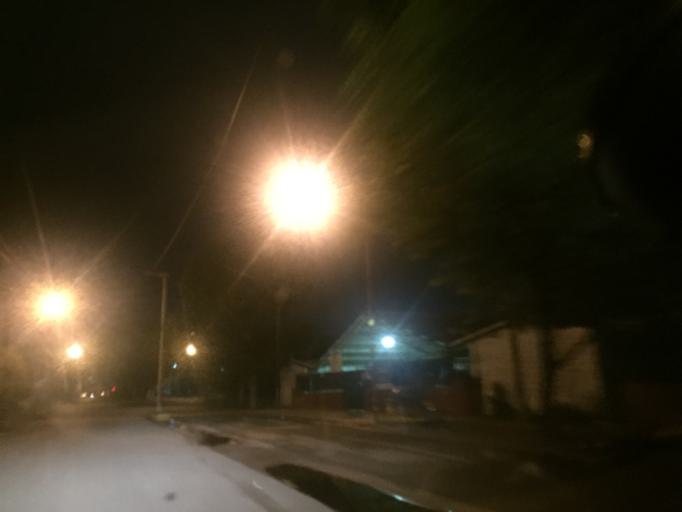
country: AR
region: Cordoba
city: Villa Allende
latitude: -31.3062
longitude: -64.2849
